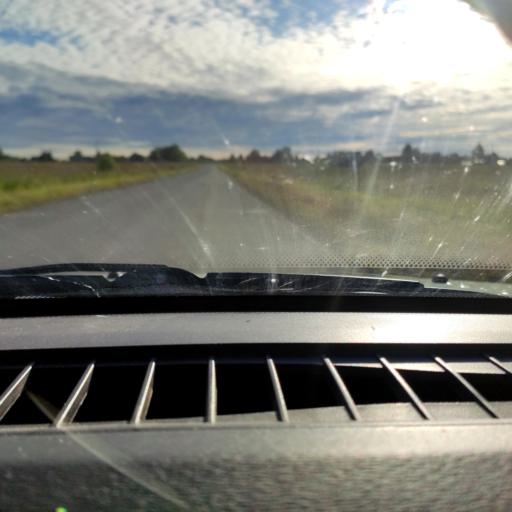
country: RU
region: Perm
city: Uinskoye
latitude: 57.0908
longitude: 56.6330
